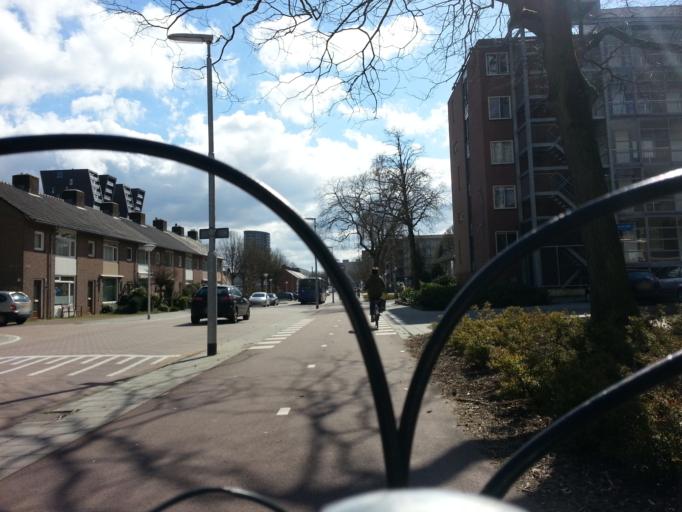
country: NL
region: North Brabant
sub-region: Gemeente Eindhoven
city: Villapark
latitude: 51.4621
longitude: 5.4883
